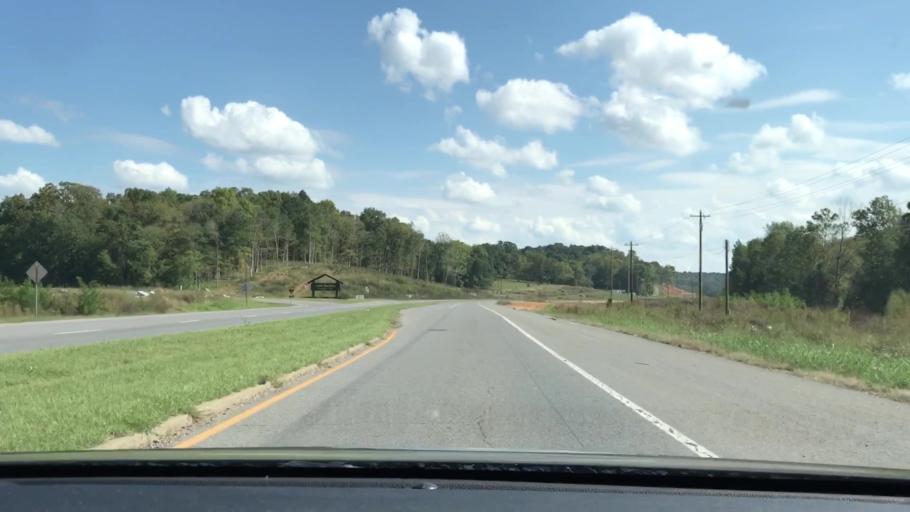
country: US
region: Kentucky
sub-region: Trigg County
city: Cadiz
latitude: 36.8051
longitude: -87.9290
